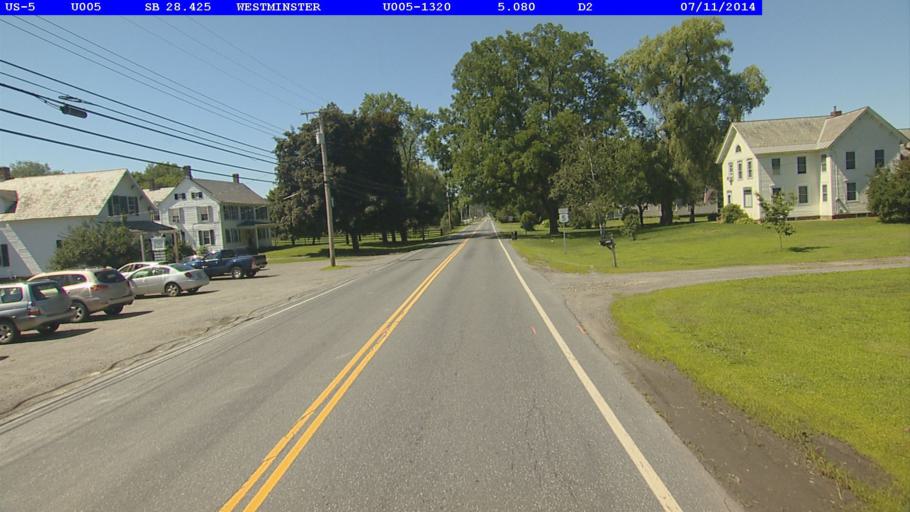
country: US
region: Vermont
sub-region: Windham County
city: Bellows Falls
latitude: 43.0847
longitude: -72.4398
